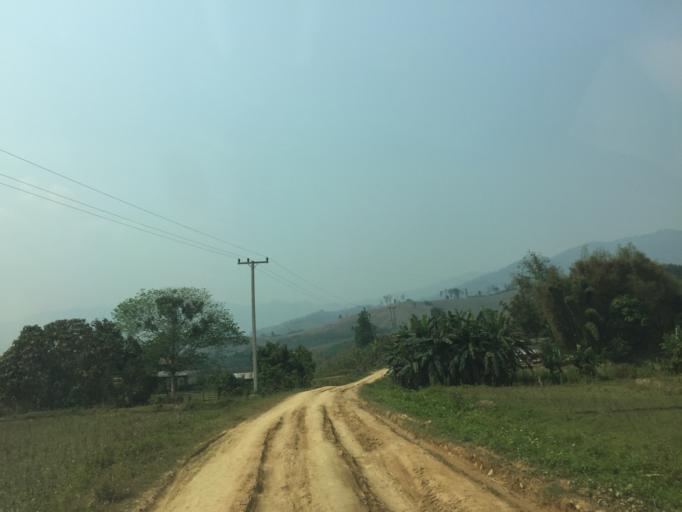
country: TH
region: Phayao
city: Phu Sang
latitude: 19.5941
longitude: 100.5285
